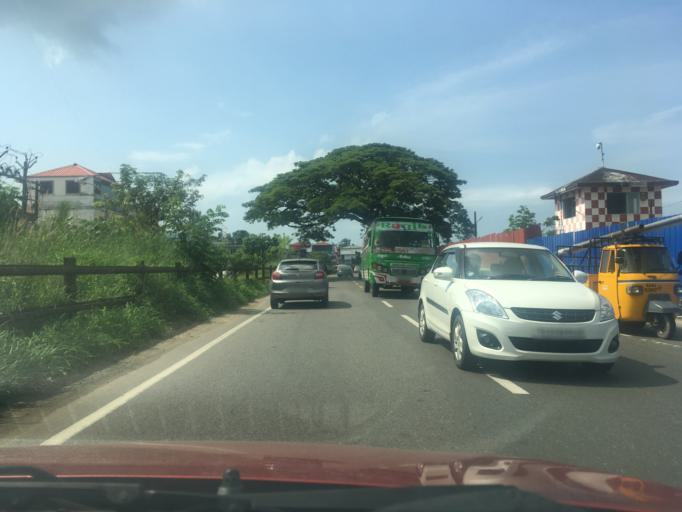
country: IN
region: Kerala
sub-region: Ernakulam
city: Cochin
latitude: 9.9385
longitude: 76.2800
